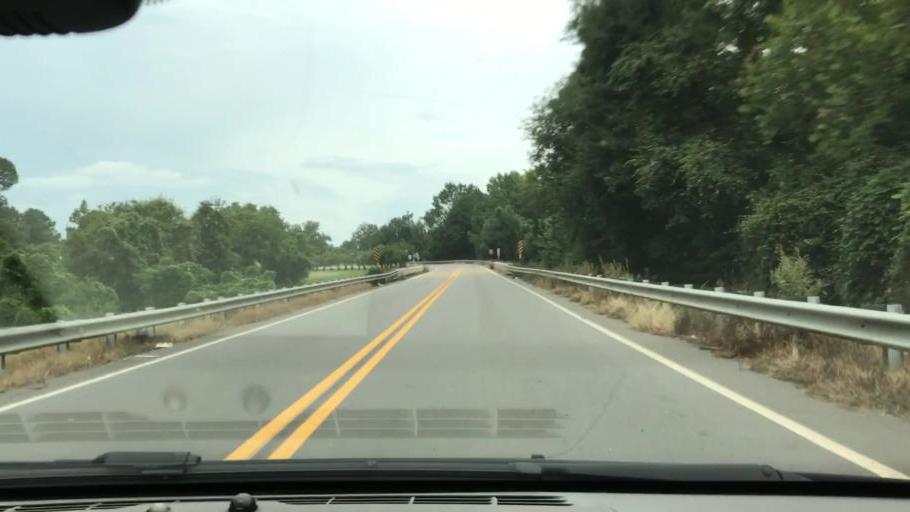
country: US
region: Alabama
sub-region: Houston County
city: Ashford
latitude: 31.2900
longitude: -85.1037
